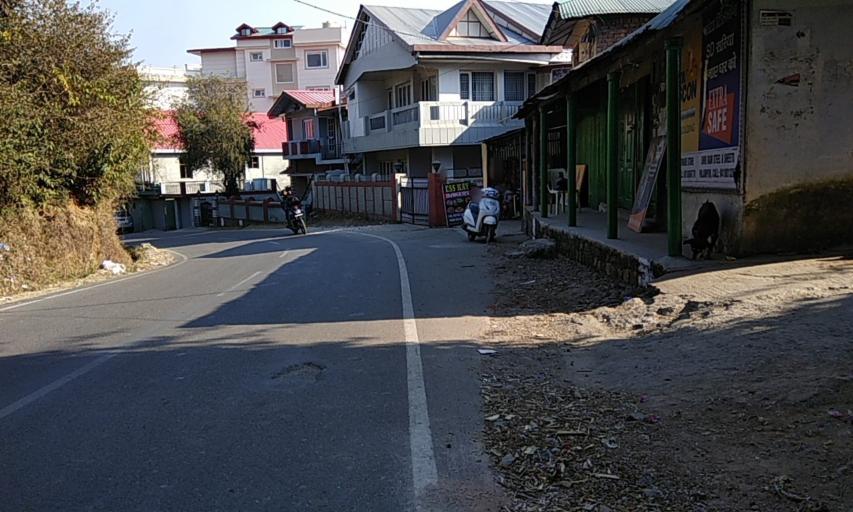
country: IN
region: Himachal Pradesh
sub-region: Kangra
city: Palampur
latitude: 32.1133
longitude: 76.5247
